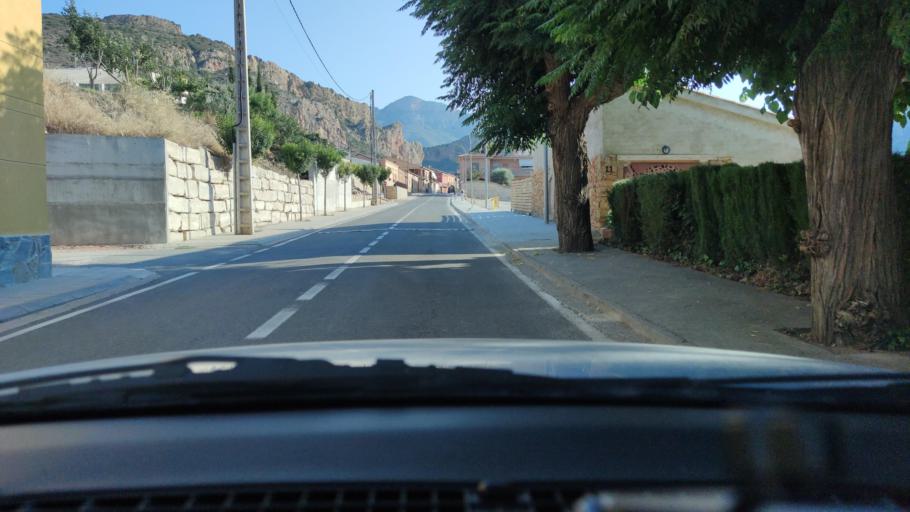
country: ES
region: Catalonia
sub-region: Provincia de Lleida
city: Camarasa
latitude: 41.8660
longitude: 0.8405
